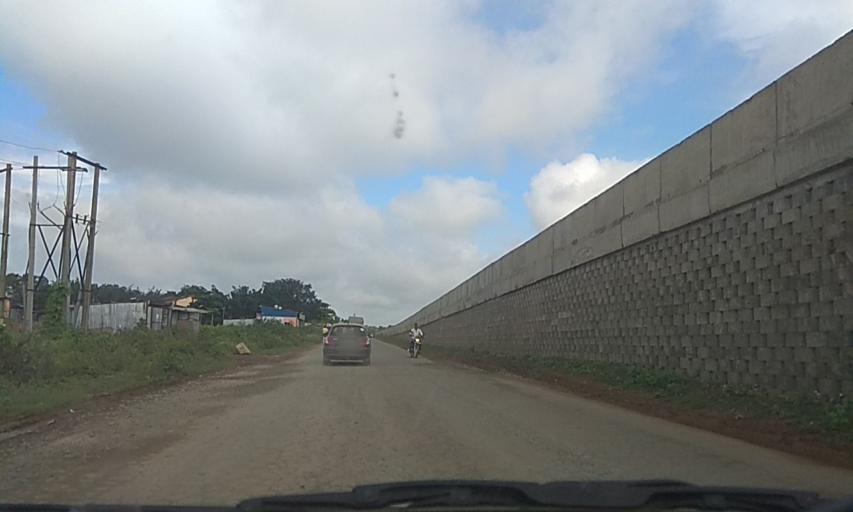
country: IN
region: Karnataka
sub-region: Haveri
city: Shiggaon
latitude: 14.9940
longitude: 75.2138
